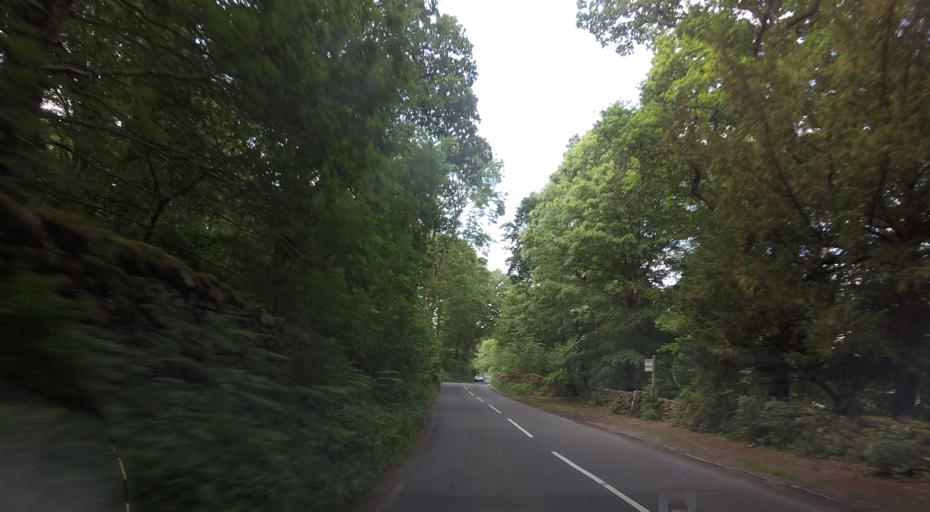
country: GB
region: England
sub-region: Cumbria
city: Keswick
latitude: 54.5826
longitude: -3.1296
